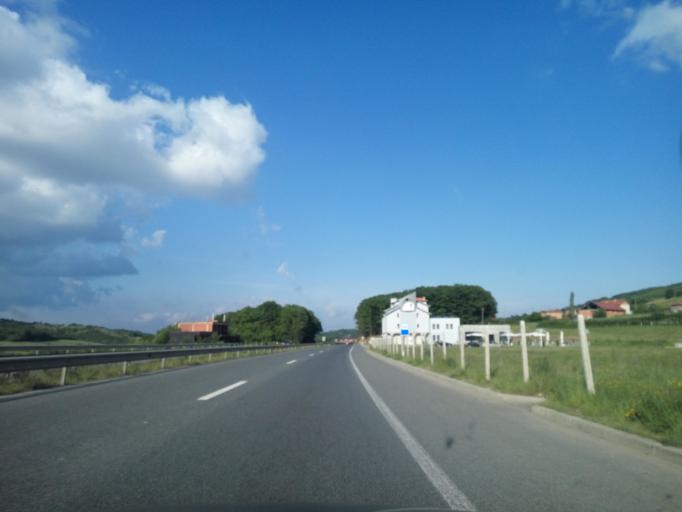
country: XK
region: Prizren
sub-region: Komuna e Malisheves
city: Llazice
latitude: 42.5682
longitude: 20.8372
